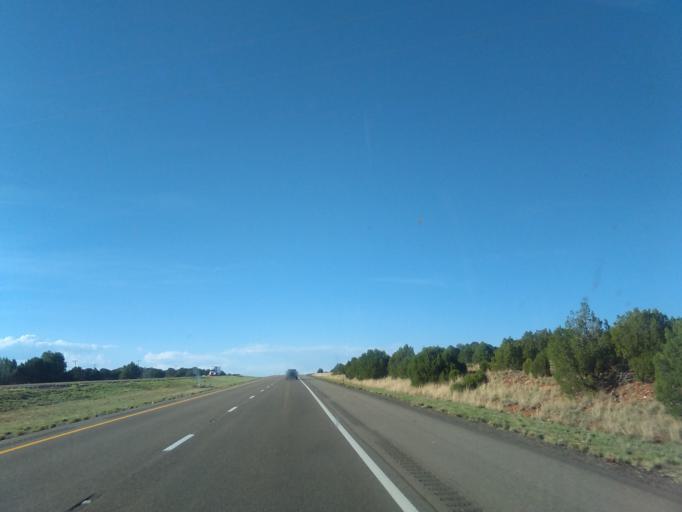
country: US
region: New Mexico
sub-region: San Miguel County
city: Las Vegas
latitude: 35.4731
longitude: -105.2751
